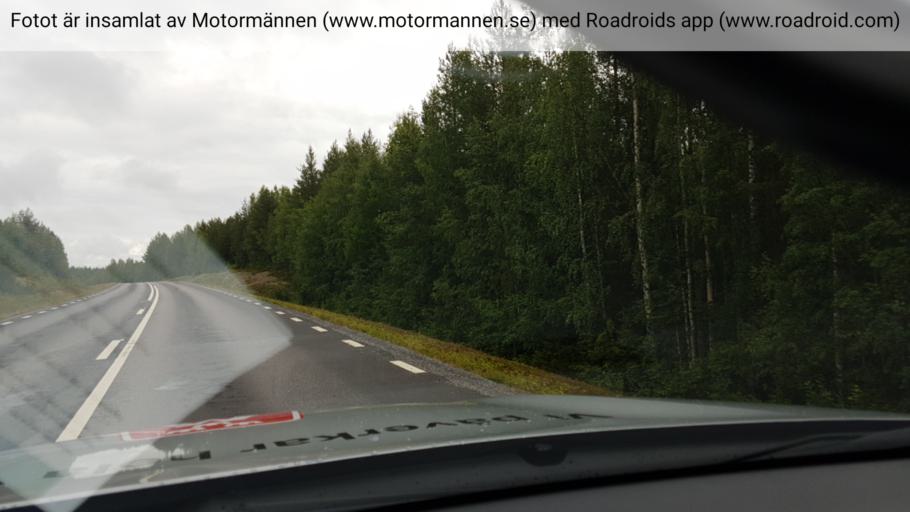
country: SE
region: Norrbotten
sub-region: Alvsbyns Kommun
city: AElvsbyn
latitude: 66.3651
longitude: 20.7260
